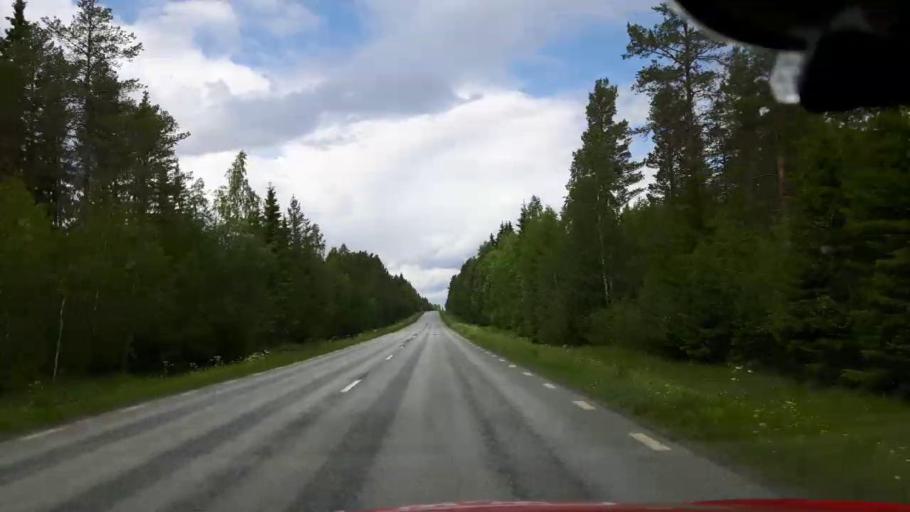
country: SE
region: Jaemtland
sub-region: Krokoms Kommun
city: Krokom
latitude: 63.3644
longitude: 14.3953
